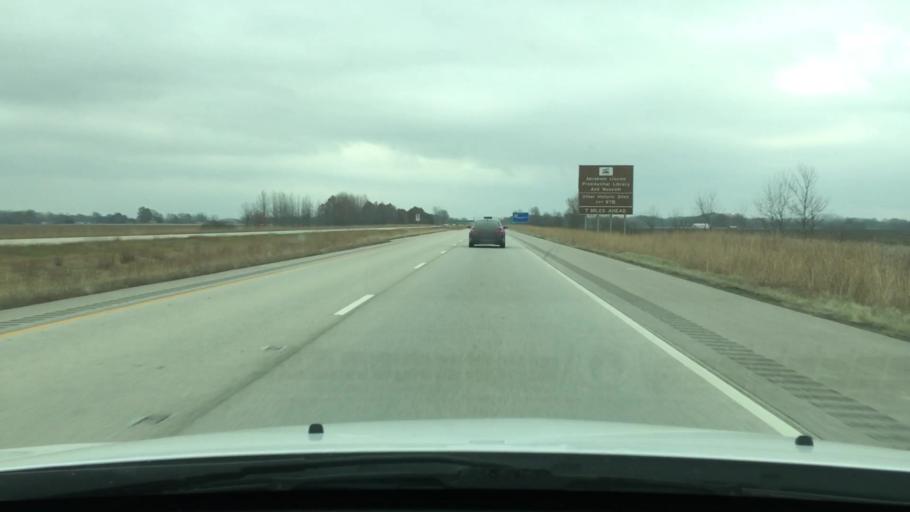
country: US
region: Illinois
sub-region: Sangamon County
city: Jerome
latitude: 39.7516
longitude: -89.7837
